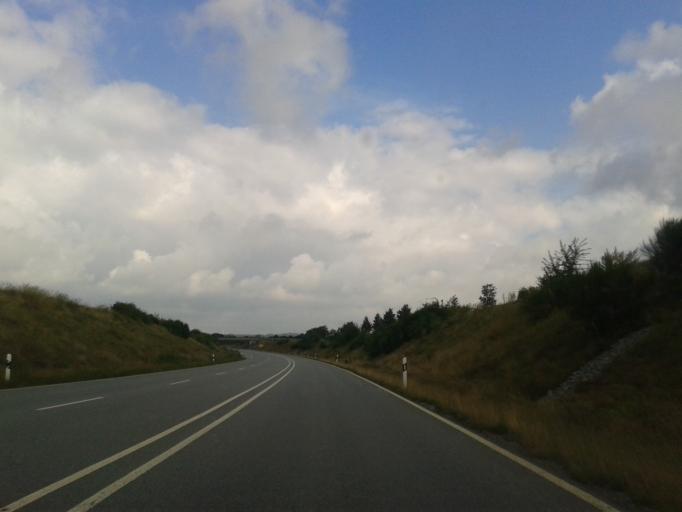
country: DE
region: Saxony
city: Radeberg
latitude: 51.0989
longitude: 13.9396
